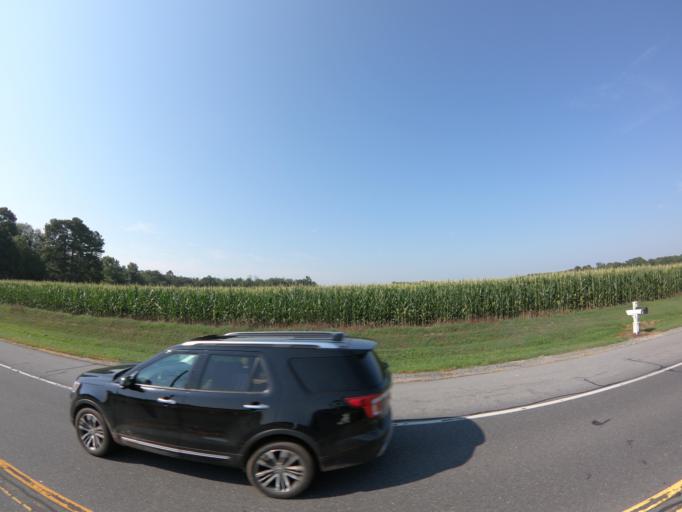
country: US
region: Delaware
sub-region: Sussex County
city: Bridgeville
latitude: 38.7966
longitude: -75.6965
